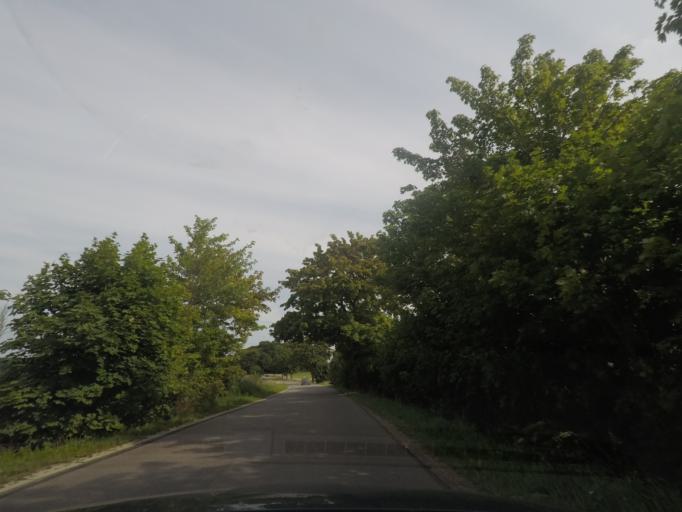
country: PL
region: Pomeranian Voivodeship
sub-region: Slupsk
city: Slupsk
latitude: 54.6016
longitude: 17.0511
